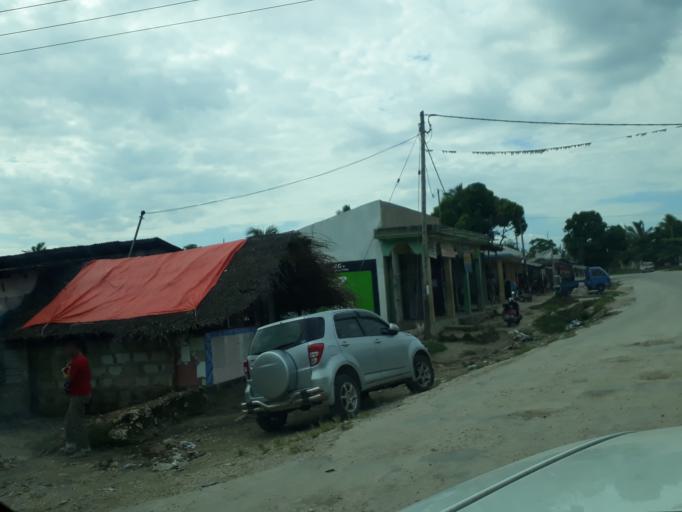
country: TZ
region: Zanzibar Central/South
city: Koani
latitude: -6.0891
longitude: 39.2226
